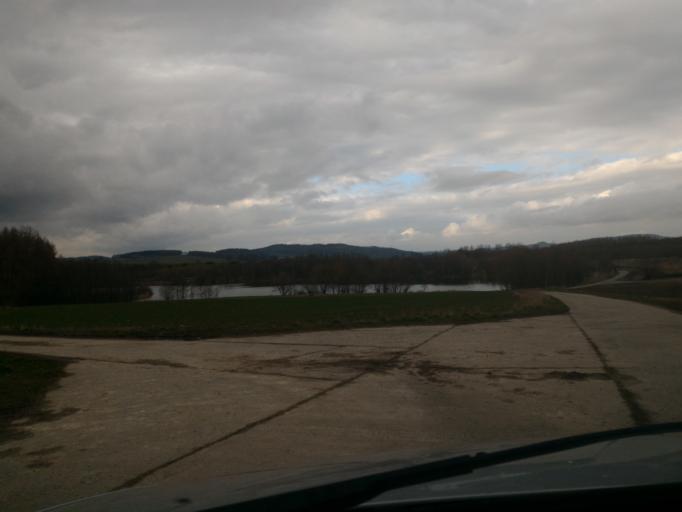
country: DE
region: Saxony
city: Olbersdorf
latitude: 50.8764
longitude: 14.7566
